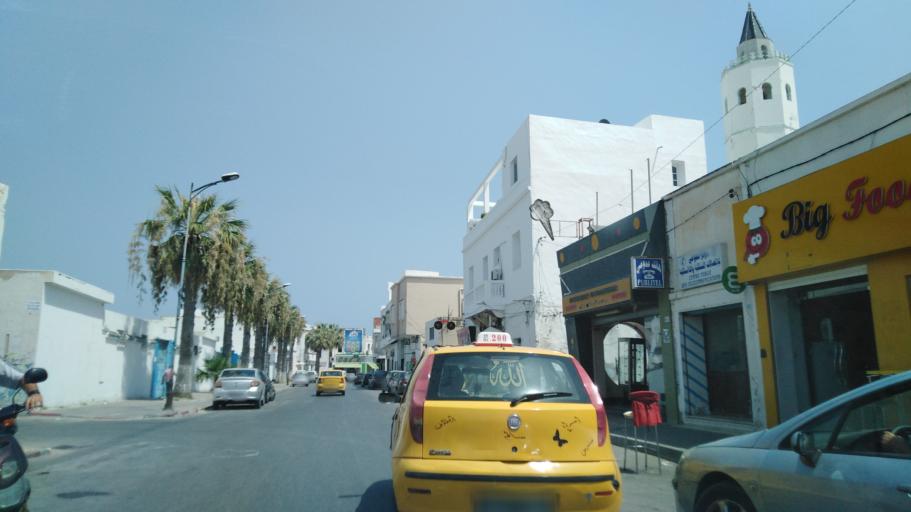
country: TN
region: Al Mahdiyah
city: Mahdia
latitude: 35.5047
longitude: 11.0647
